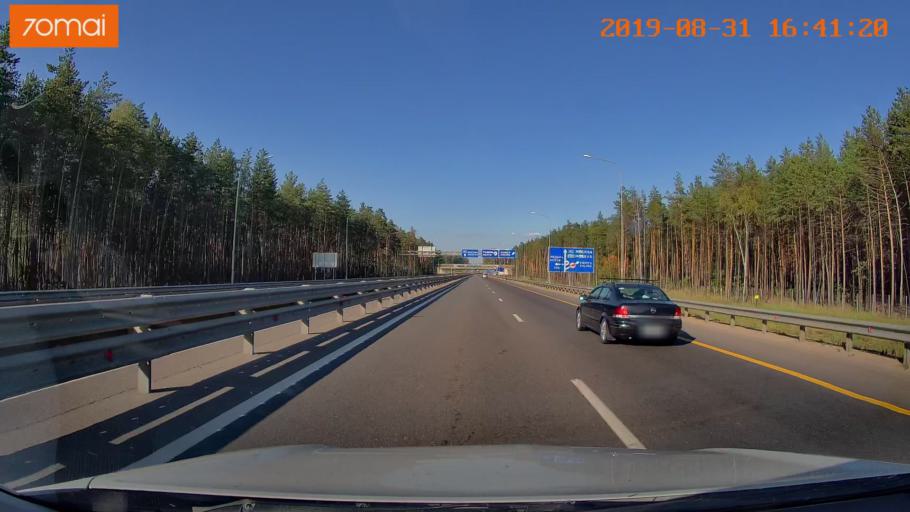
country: RU
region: Kaluga
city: Mstikhino
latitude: 54.5785
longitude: 36.0654
